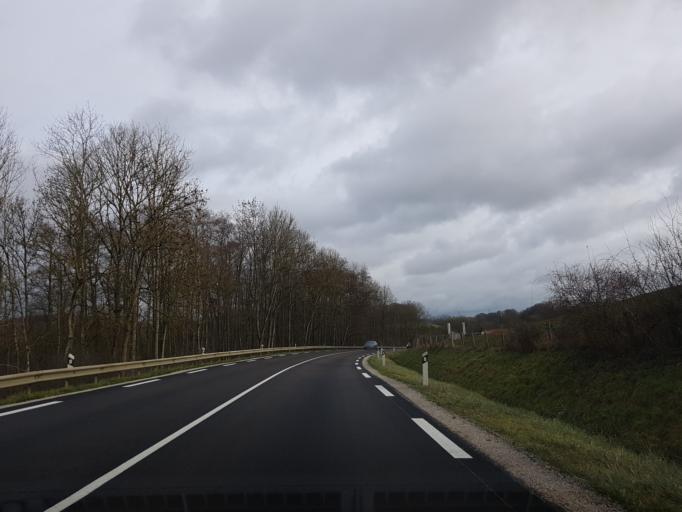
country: FR
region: Champagne-Ardenne
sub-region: Departement de la Haute-Marne
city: Langres
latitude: 47.8577
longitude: 5.3650
